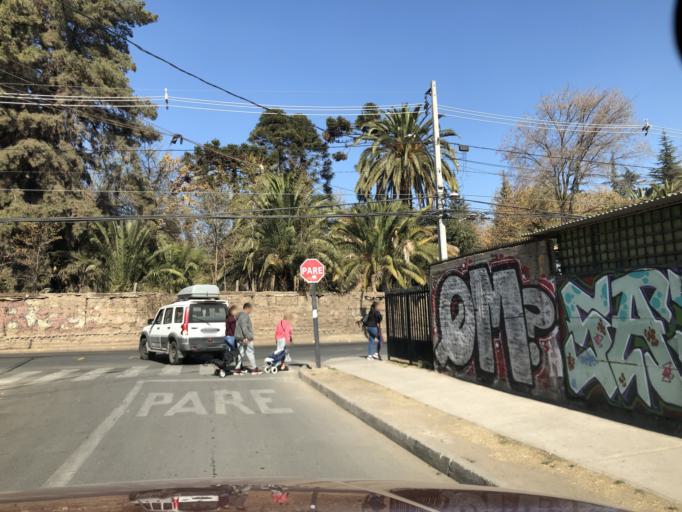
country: CL
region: Santiago Metropolitan
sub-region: Provincia de Cordillera
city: Puente Alto
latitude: -33.5689
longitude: -70.5817
